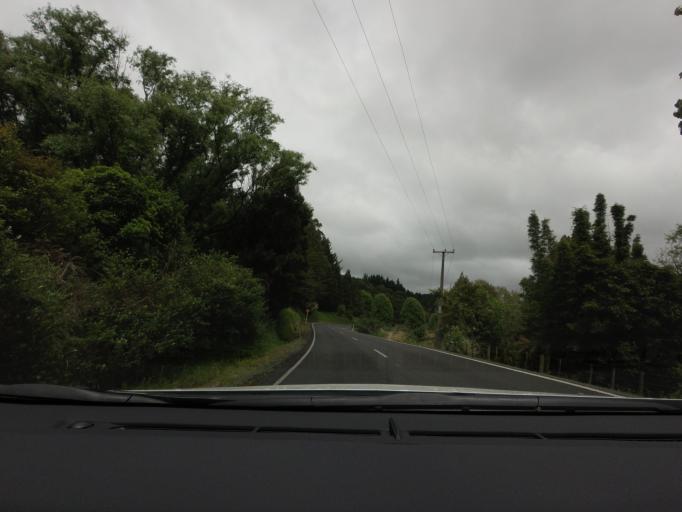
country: NZ
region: Auckland
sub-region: Auckland
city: Warkworth
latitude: -36.5032
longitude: 174.6409
